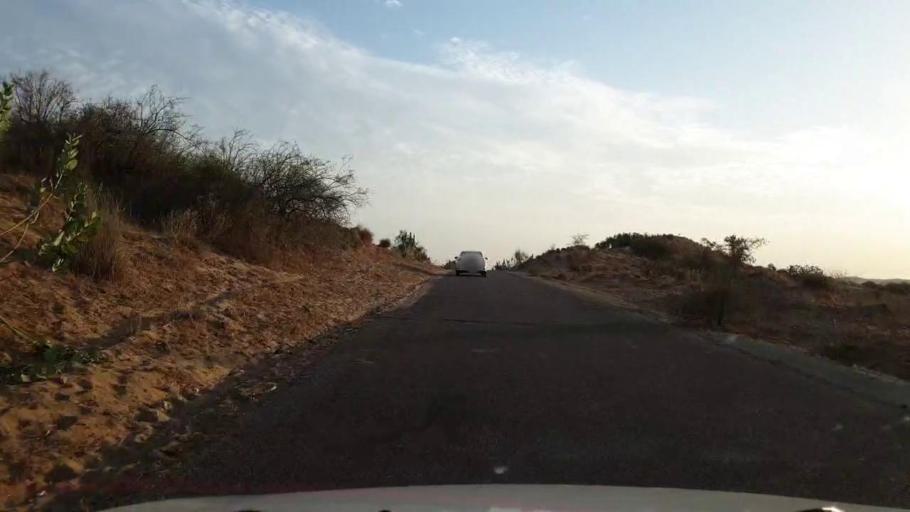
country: PK
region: Sindh
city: Nabisar
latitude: 25.0170
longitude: 69.9391
